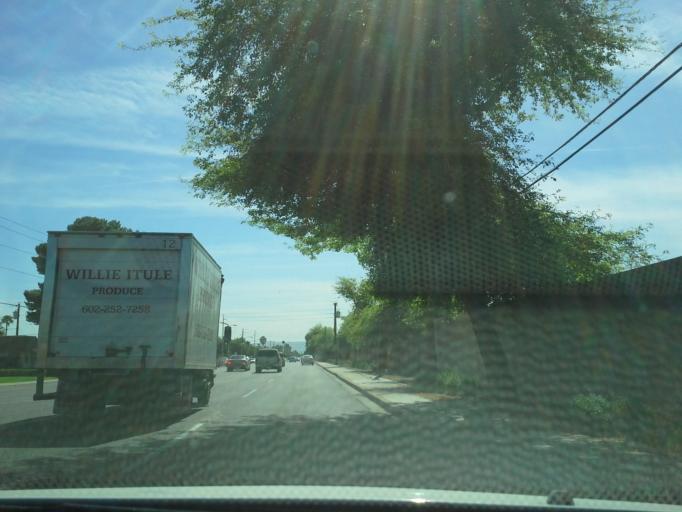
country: US
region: Arizona
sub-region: Maricopa County
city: Phoenix
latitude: 33.5366
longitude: -112.0476
